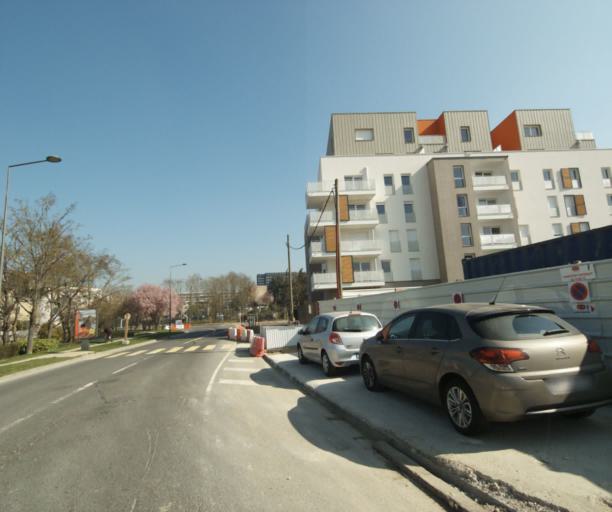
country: FR
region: Ile-de-France
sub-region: Departement du Val-d'Oise
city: Cergy
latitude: 49.0392
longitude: 2.0686
